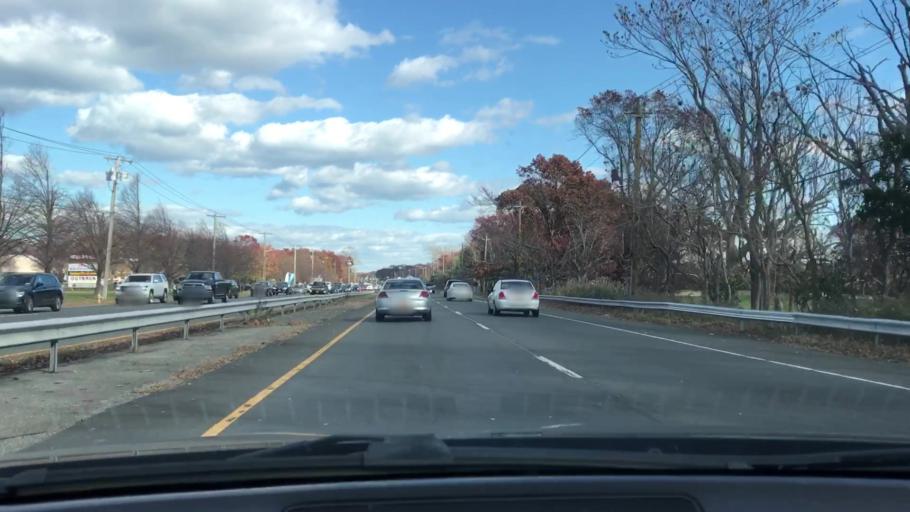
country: US
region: New York
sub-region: Suffolk County
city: Terryville
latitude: 40.9051
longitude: -73.0713
